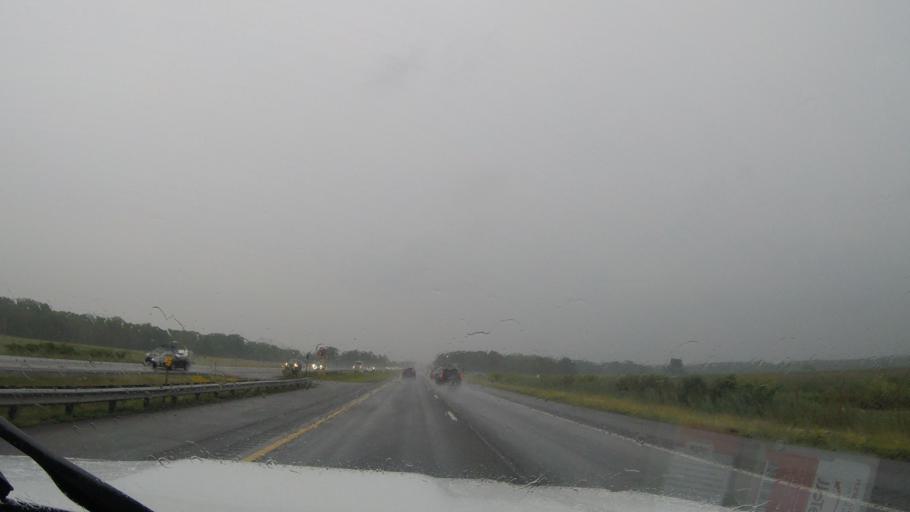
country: US
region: New York
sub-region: Seneca County
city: Bridgeport
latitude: 42.9932
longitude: -76.7467
